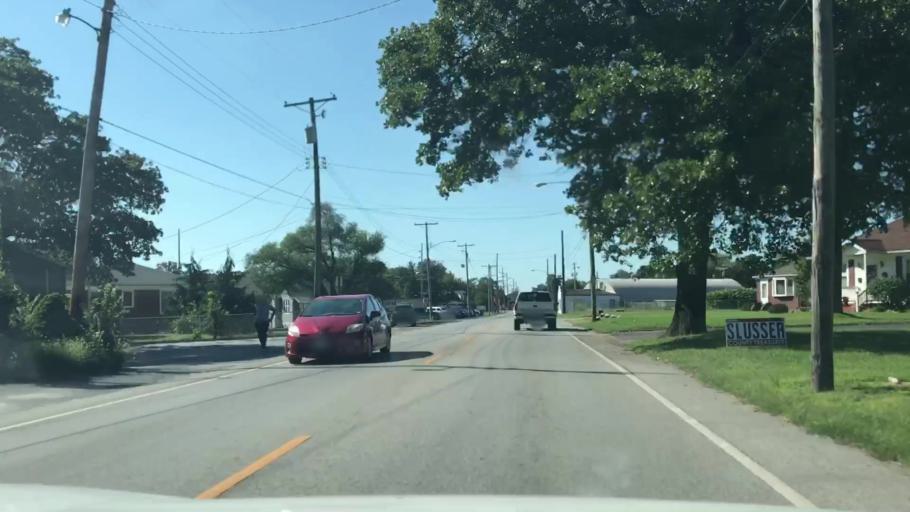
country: US
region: Illinois
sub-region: Madison County
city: Wood River
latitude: 38.8666
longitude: -90.0847
